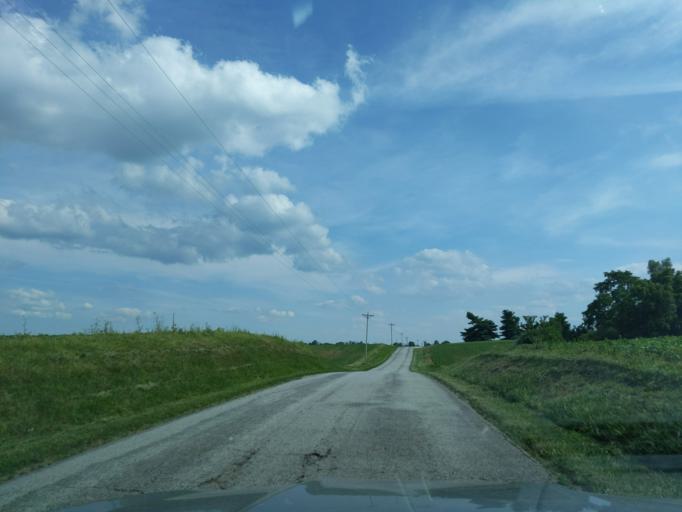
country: US
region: Indiana
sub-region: Decatur County
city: Greensburg
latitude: 39.2817
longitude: -85.4656
